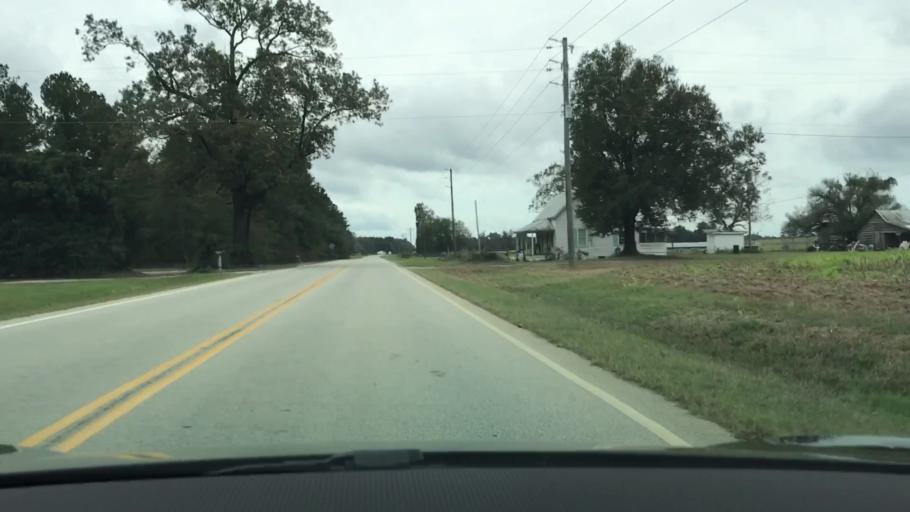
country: US
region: Georgia
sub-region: Jefferson County
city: Wrens
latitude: 33.1776
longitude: -82.4534
